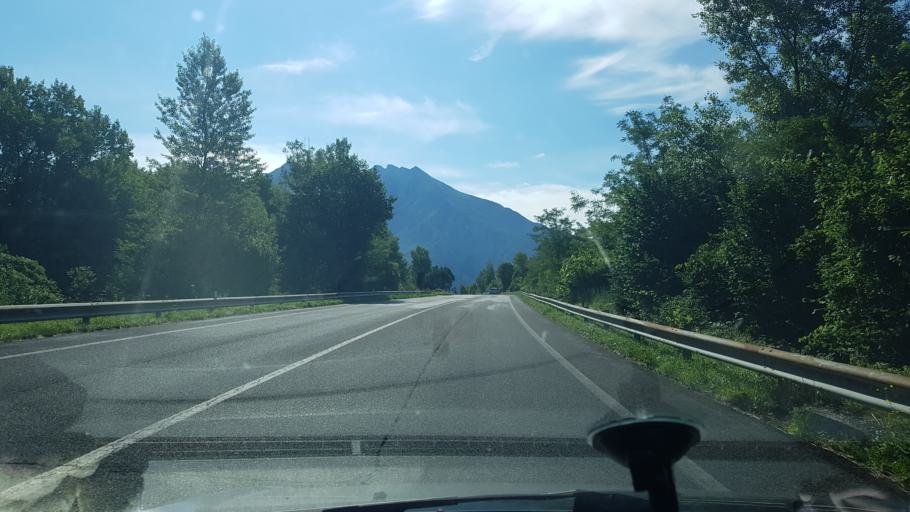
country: IT
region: Friuli Venezia Giulia
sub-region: Provincia di Udine
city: Amaro
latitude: 46.3729
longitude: 13.0791
